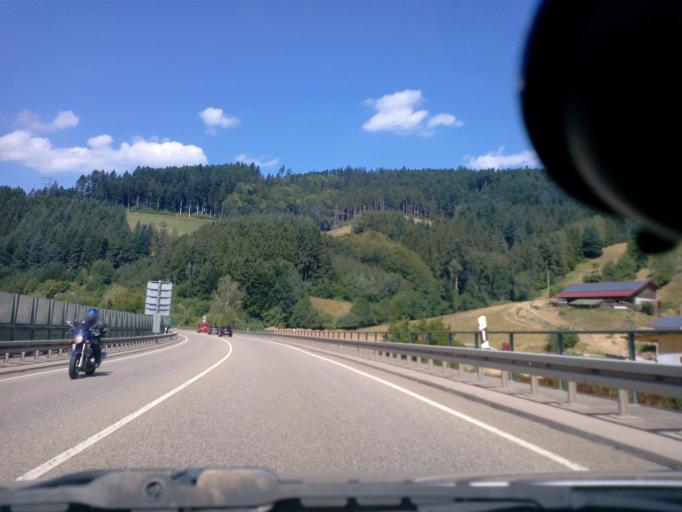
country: DE
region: Baden-Wuerttemberg
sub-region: Freiburg Region
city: Hausach
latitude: 48.2882
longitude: 8.1879
